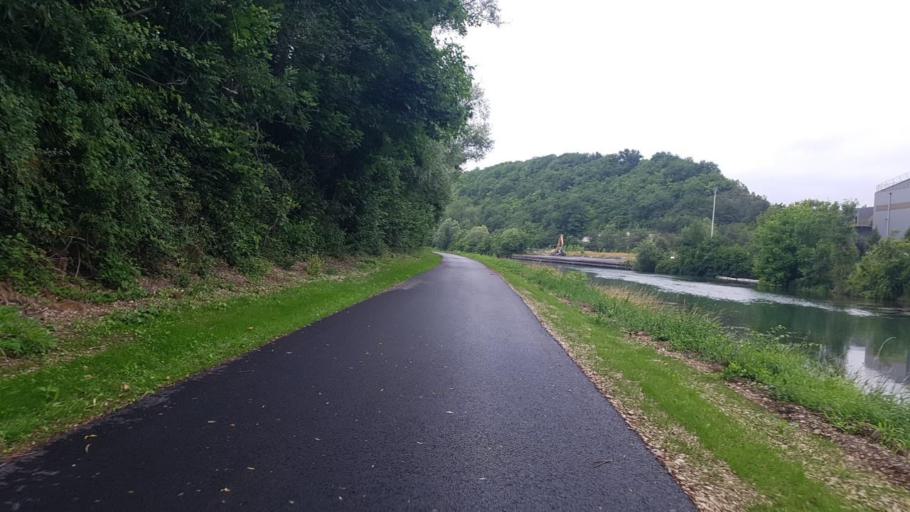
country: FR
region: Champagne-Ardenne
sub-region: Departement de la Marne
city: Vitry-le-Francois
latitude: 48.7667
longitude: 4.5590
